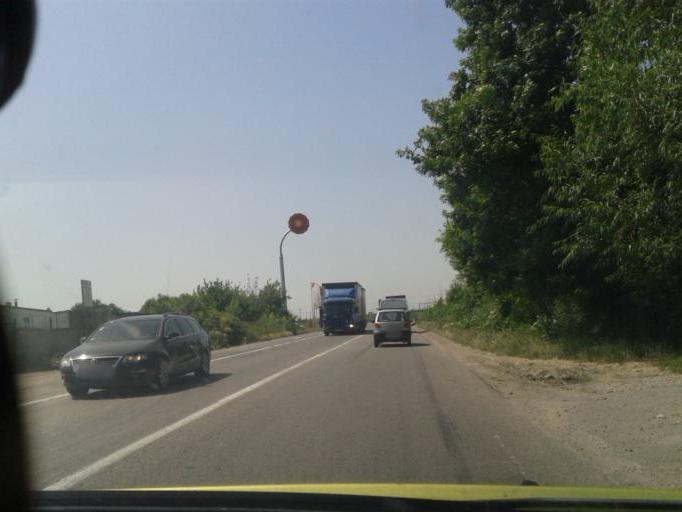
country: RO
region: Ilfov
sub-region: Comuna Glina
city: Catelu
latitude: 44.4137
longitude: 26.2357
